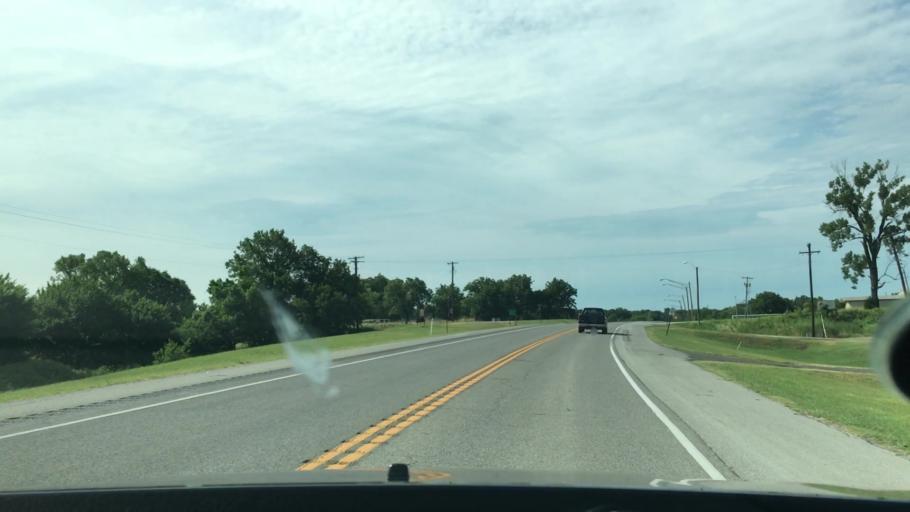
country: US
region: Oklahoma
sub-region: Murray County
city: Sulphur
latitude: 34.5221
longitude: -96.9691
